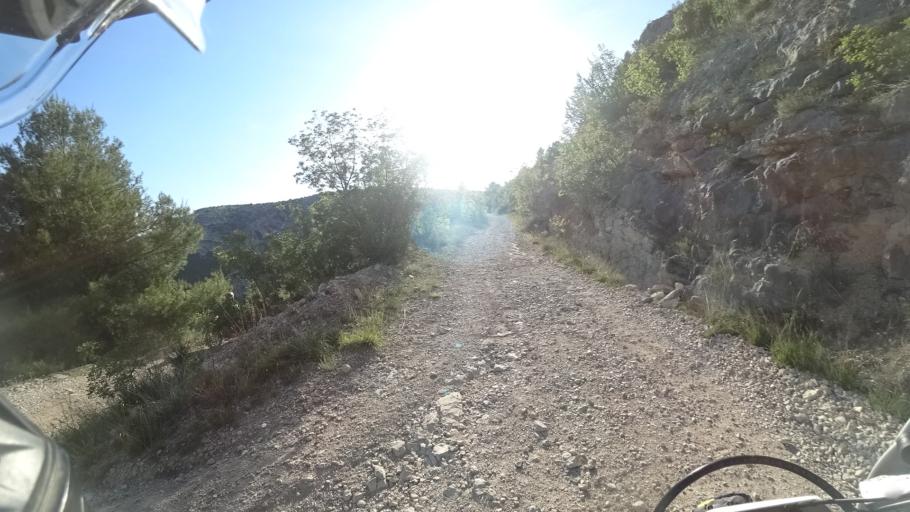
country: HR
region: Sibensko-Kniniska
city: Drnis
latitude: 43.8293
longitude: 16.0227
